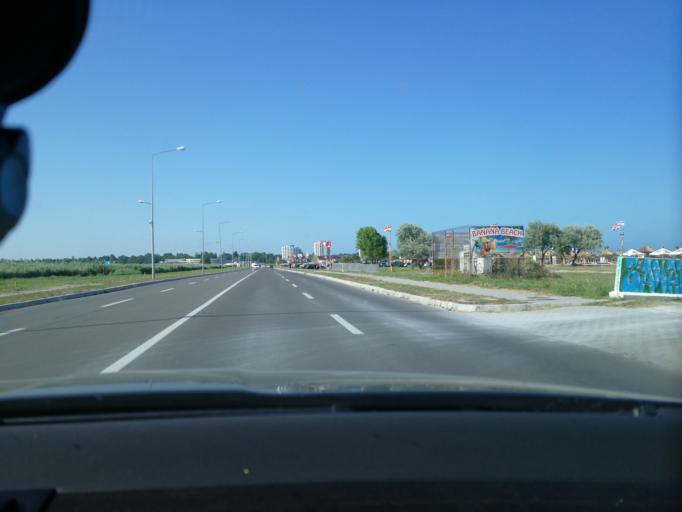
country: RO
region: Constanta
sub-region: Municipiul Mangalia
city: Mangalia
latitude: 43.8362
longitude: 28.5891
